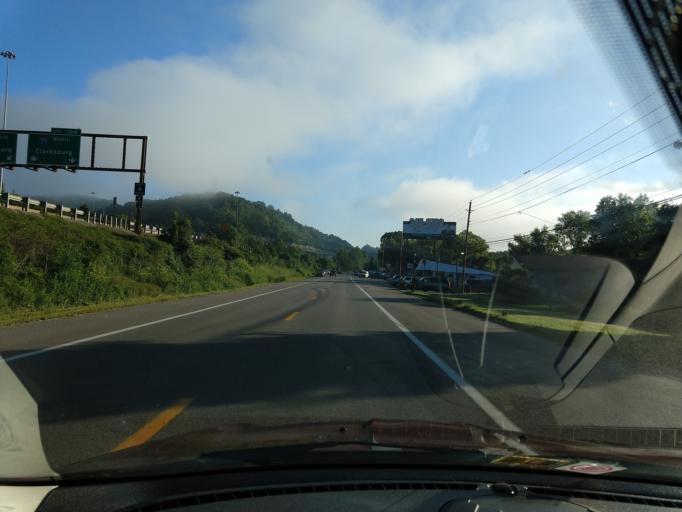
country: US
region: West Virginia
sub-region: Kanawha County
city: Charleston
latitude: 38.3770
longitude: -81.6035
